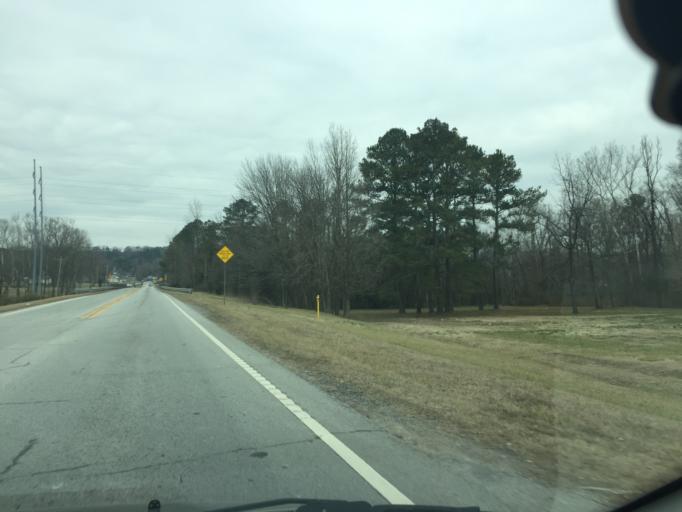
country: US
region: Georgia
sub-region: Catoosa County
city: Indian Springs
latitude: 34.9636
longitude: -85.1743
